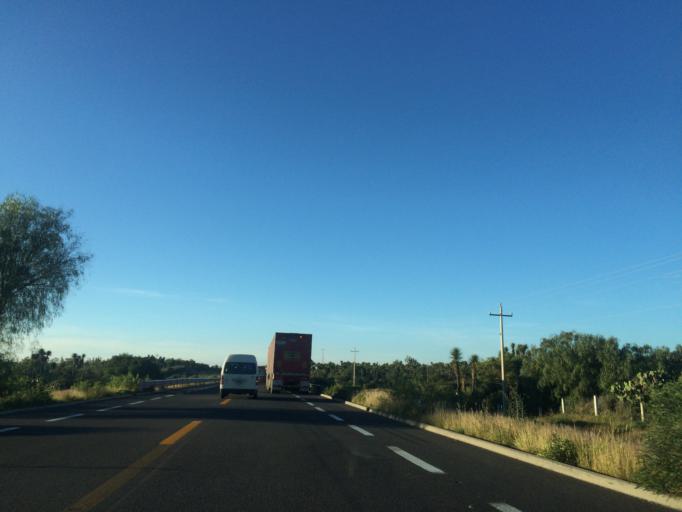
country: MX
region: Puebla
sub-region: Tehuacan
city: Magdalena Cuayucatepec
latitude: 18.5865
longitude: -97.4685
